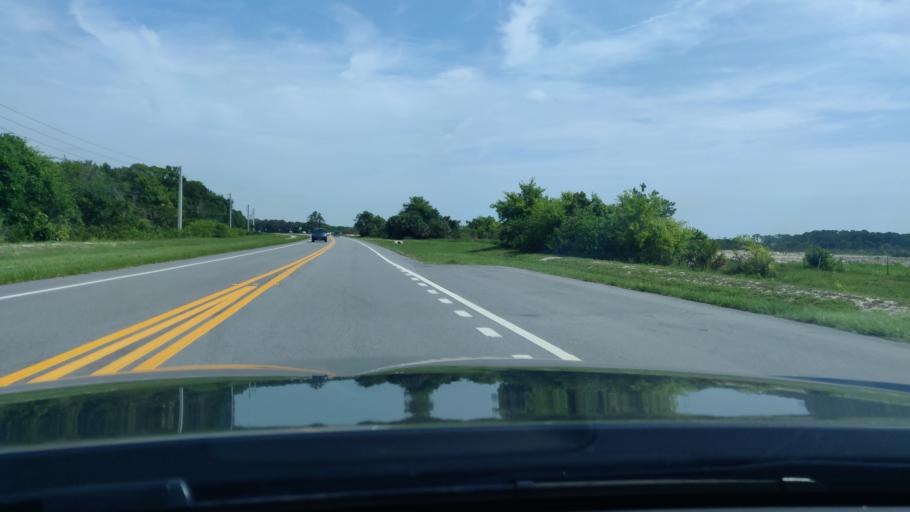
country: US
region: Florida
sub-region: Flagler County
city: Flagler Beach
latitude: 29.4964
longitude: -81.1573
